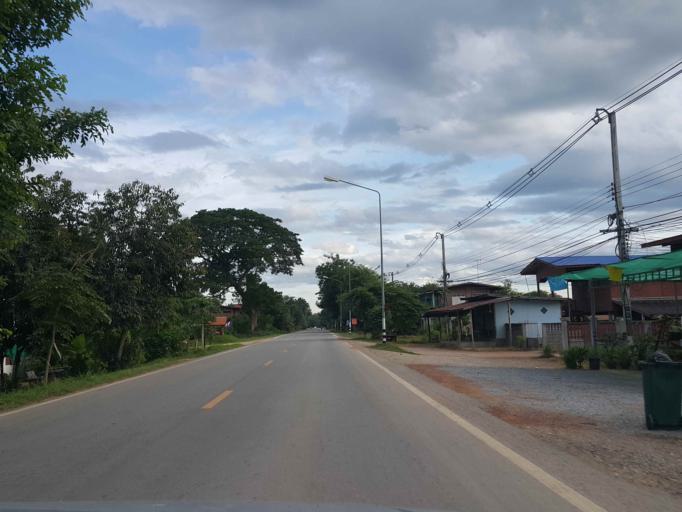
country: TH
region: Sukhothai
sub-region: Amphoe Si Satchanalai
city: Si Satchanalai
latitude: 17.5062
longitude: 99.7530
